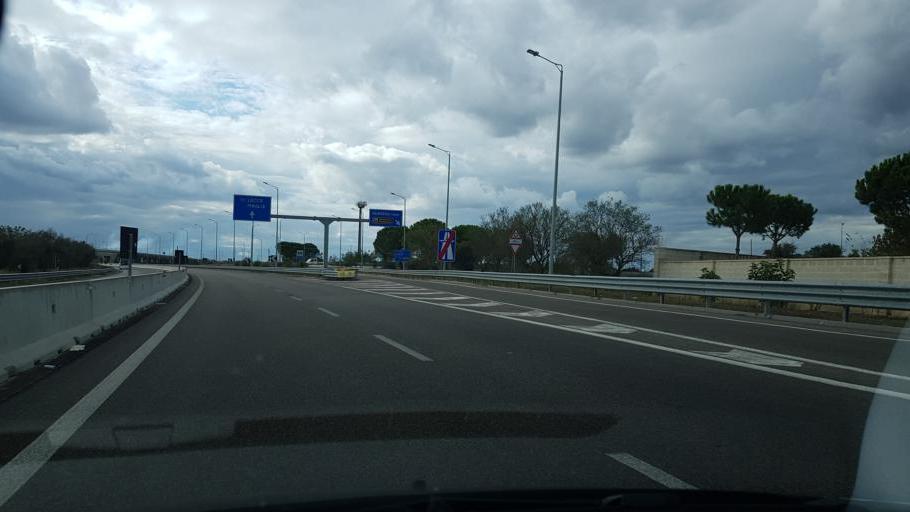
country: IT
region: Apulia
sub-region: Provincia di Lecce
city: Palmariggi
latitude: 40.1278
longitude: 18.3715
